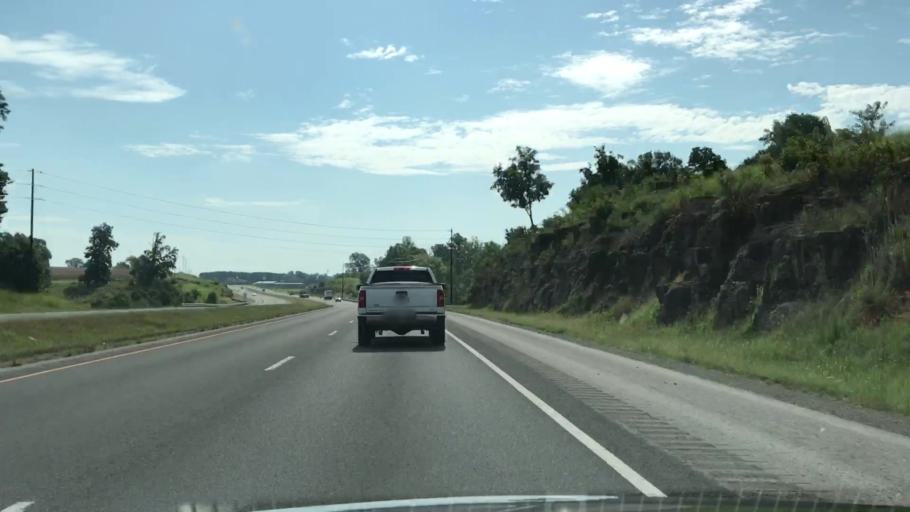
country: US
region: Kentucky
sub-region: Allen County
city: Scottsville
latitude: 36.7589
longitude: -86.2293
